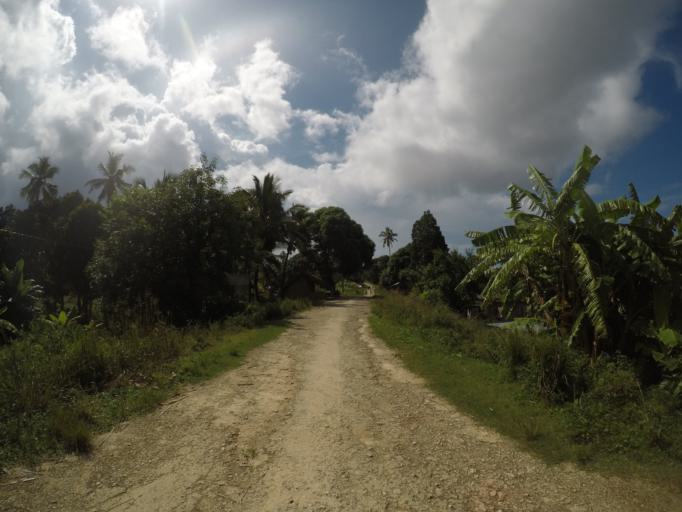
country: TZ
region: Pemba South
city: Mtambile
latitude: -5.3495
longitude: 39.6977
